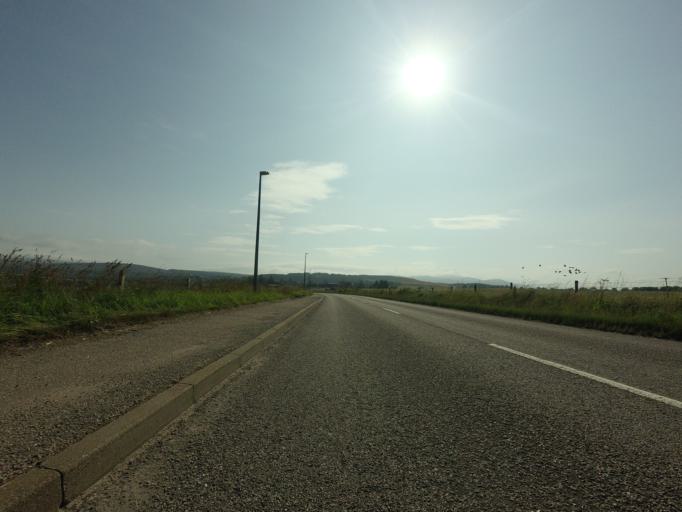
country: GB
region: Scotland
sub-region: Highland
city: Alness
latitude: 57.8871
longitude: -4.3580
